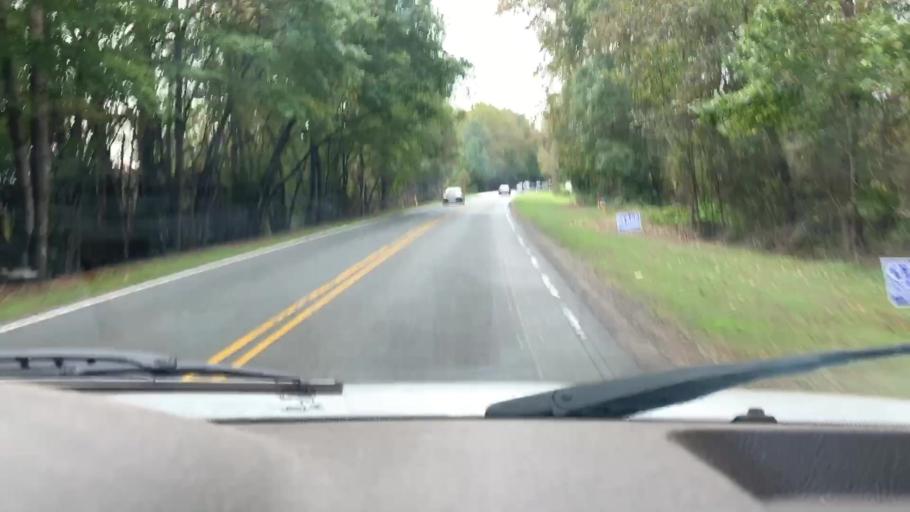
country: US
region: North Carolina
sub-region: Mecklenburg County
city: Cornelius
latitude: 35.4563
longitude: -80.8679
